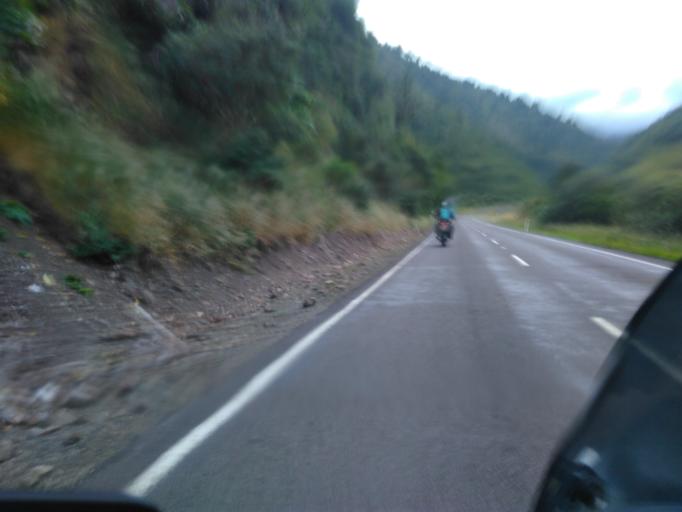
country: NZ
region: Bay of Plenty
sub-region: Opotiki District
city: Opotiki
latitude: -38.3161
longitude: 177.3958
